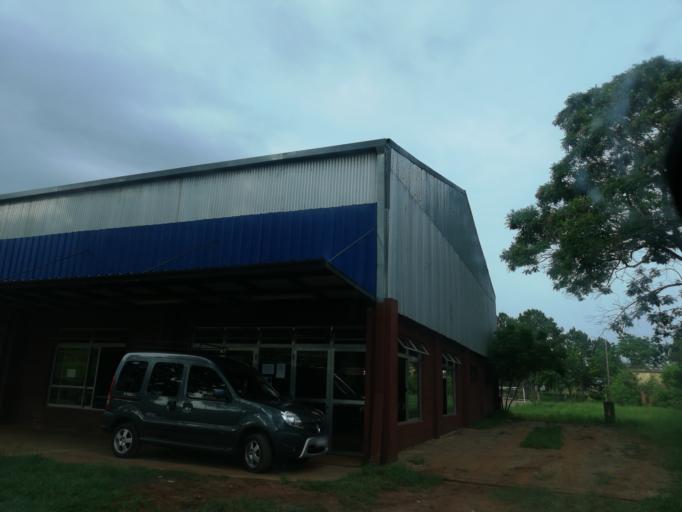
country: AR
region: Misiones
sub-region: Departamento de Capital
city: Posadas
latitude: -27.4368
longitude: -55.8901
